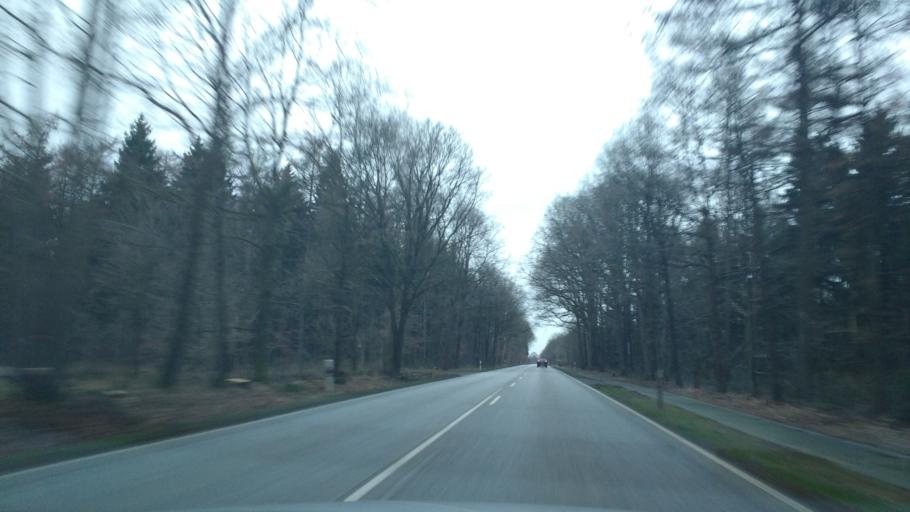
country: DE
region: Schleswig-Holstein
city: Peissen
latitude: 54.0104
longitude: 9.5889
